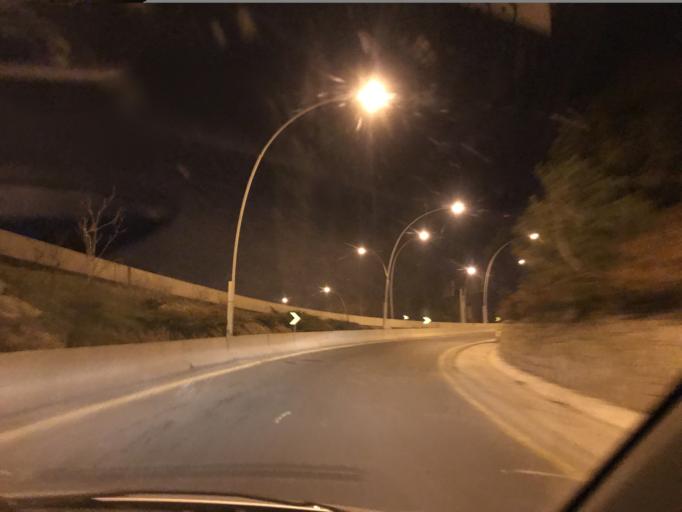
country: TR
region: Ankara
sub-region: Goelbasi
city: Golbasi
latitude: 39.8429
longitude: 32.8039
